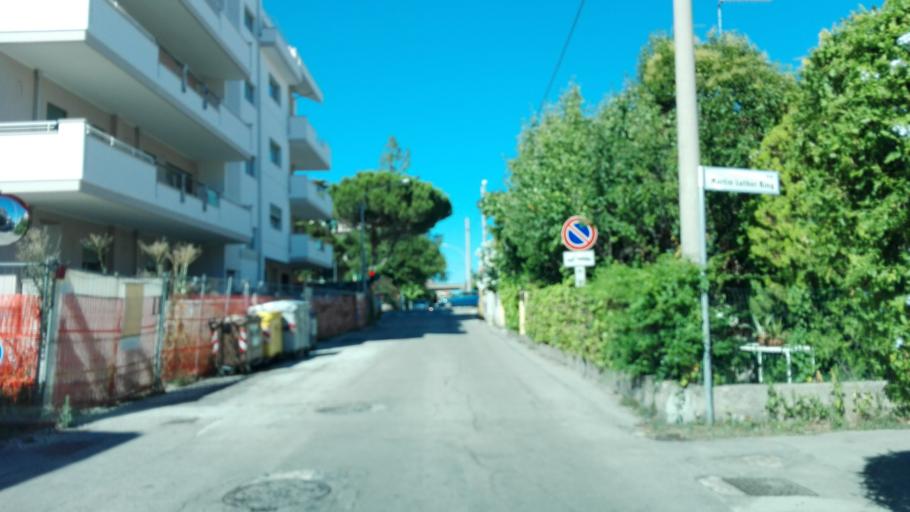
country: IT
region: Abruzzo
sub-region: Provincia di Pescara
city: Montesilvano Marina
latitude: 42.5098
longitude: 14.1570
